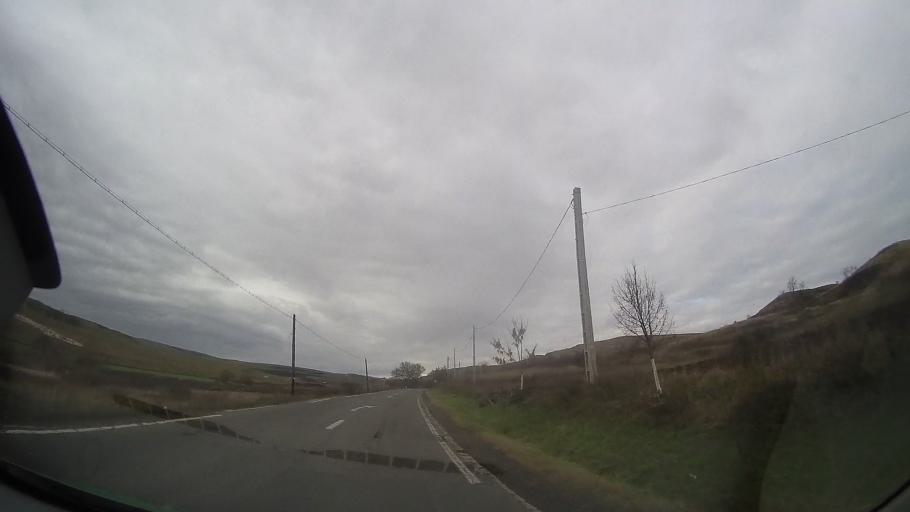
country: RO
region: Mures
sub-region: Comuna Craesti
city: Craiesti
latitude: 46.7598
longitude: 24.3987
